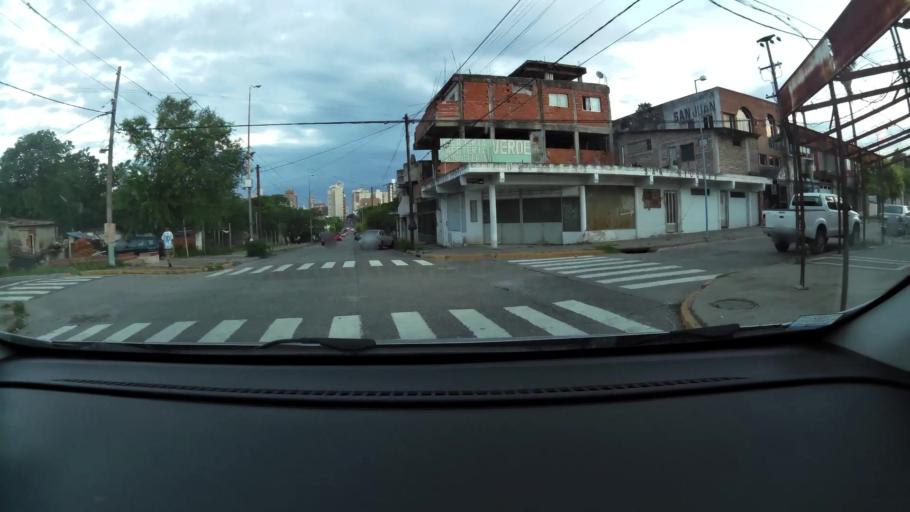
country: AR
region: Buenos Aires
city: San Nicolas de los Arroyos
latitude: -33.3235
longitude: -60.2239
